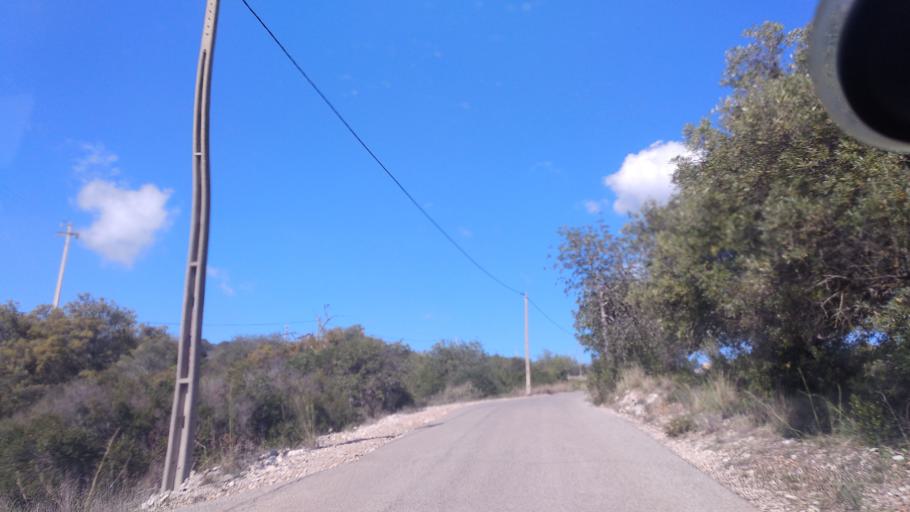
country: PT
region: Faro
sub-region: Sao Bras de Alportel
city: Sao Bras de Alportel
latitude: 37.1349
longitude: -7.9069
